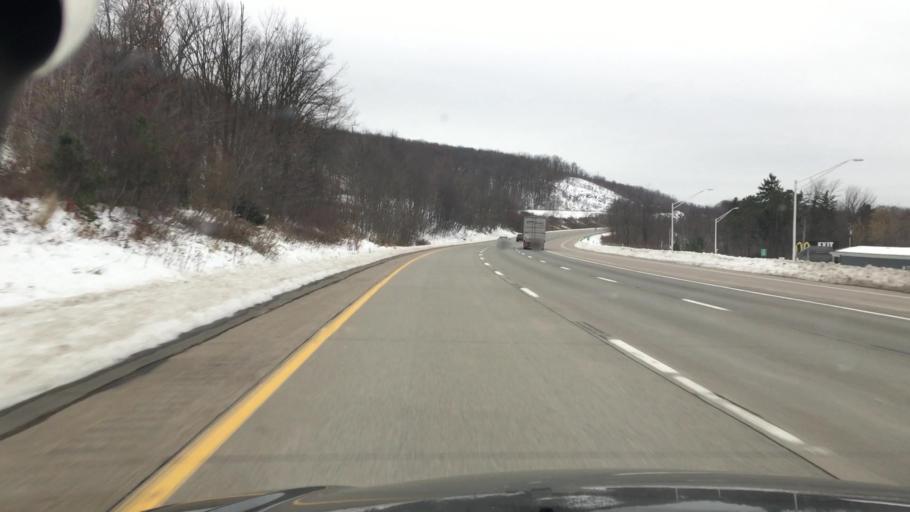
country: US
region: Pennsylvania
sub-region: Luzerne County
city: Freeland
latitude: 41.0795
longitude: -75.9666
